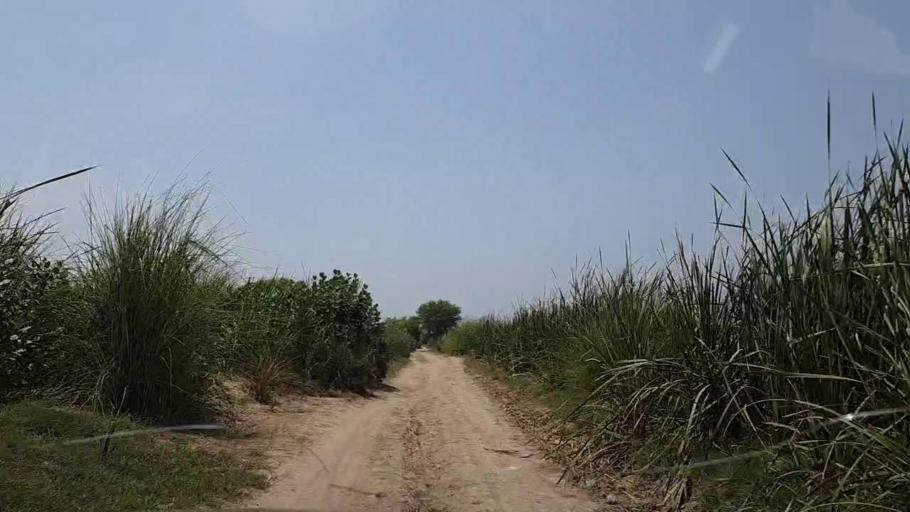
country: PK
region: Sindh
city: Khanpur
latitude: 27.7955
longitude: 69.4648
